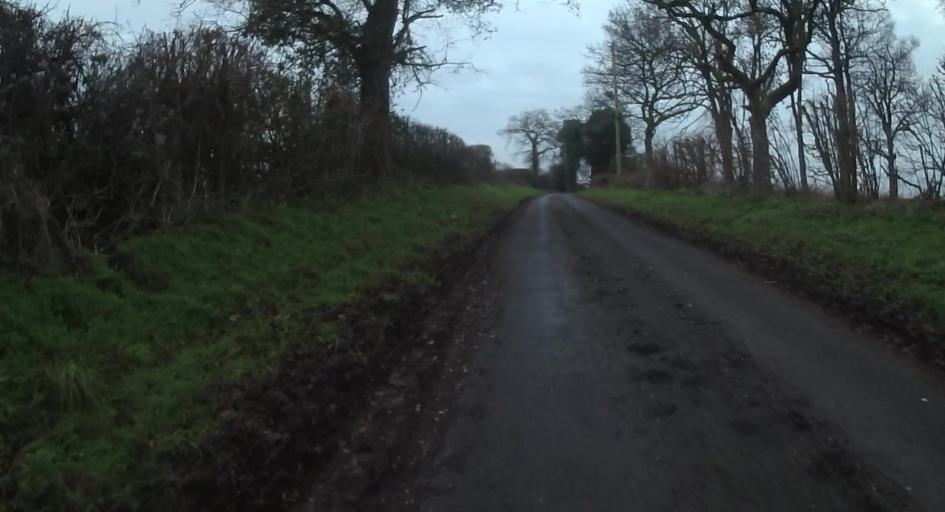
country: GB
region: England
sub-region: Hampshire
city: Overton
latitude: 51.2629
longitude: -1.3112
